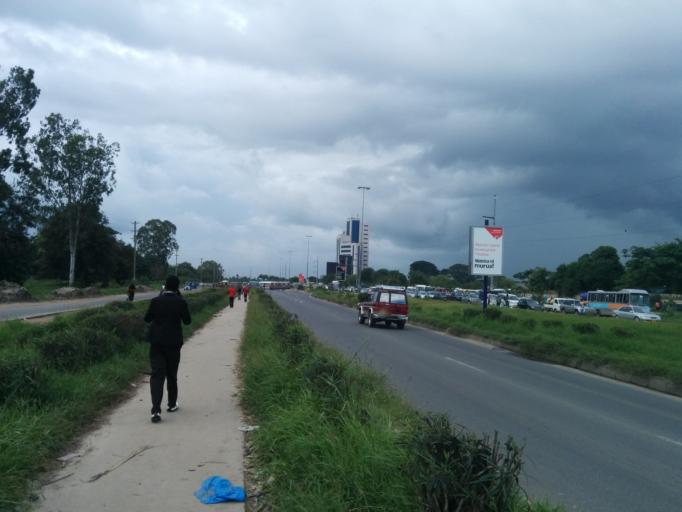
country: TZ
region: Dar es Salaam
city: Magomeni
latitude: -6.7871
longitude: 39.2097
